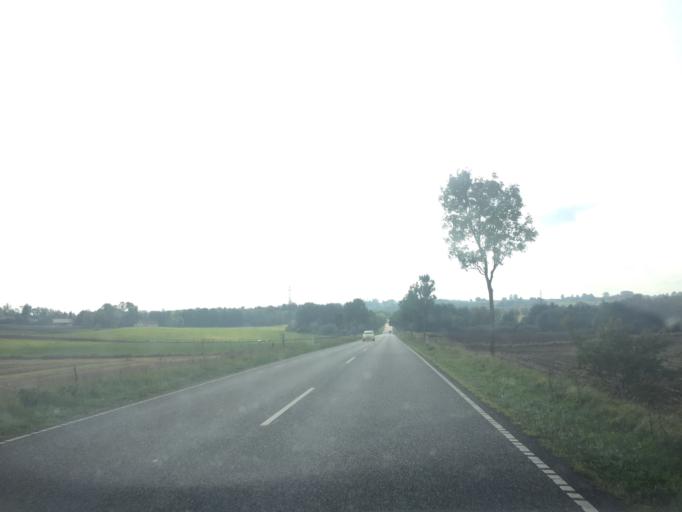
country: DK
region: Zealand
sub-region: Holbaek Kommune
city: Tollose
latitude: 55.6396
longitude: 11.8008
